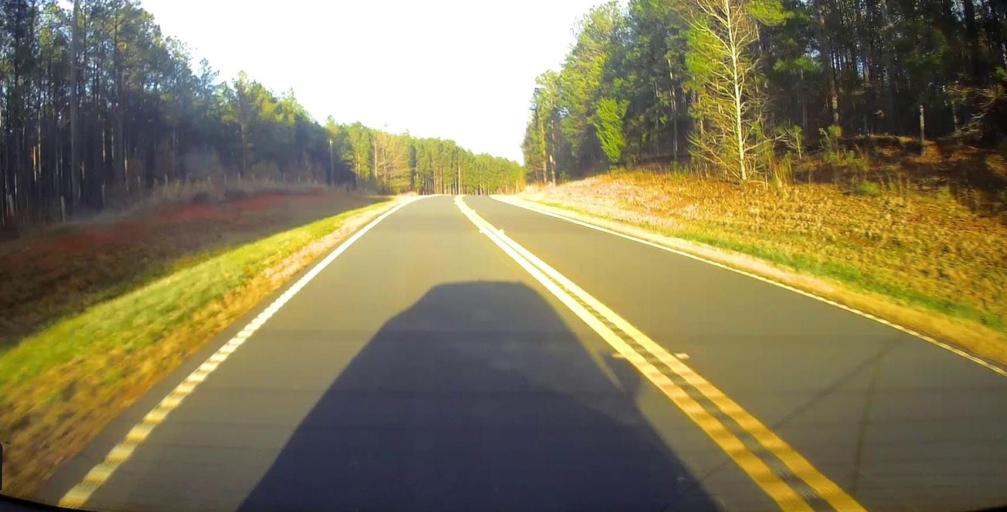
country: US
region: Georgia
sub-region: Talbot County
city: Sardis
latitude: 32.7469
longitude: -84.5916
